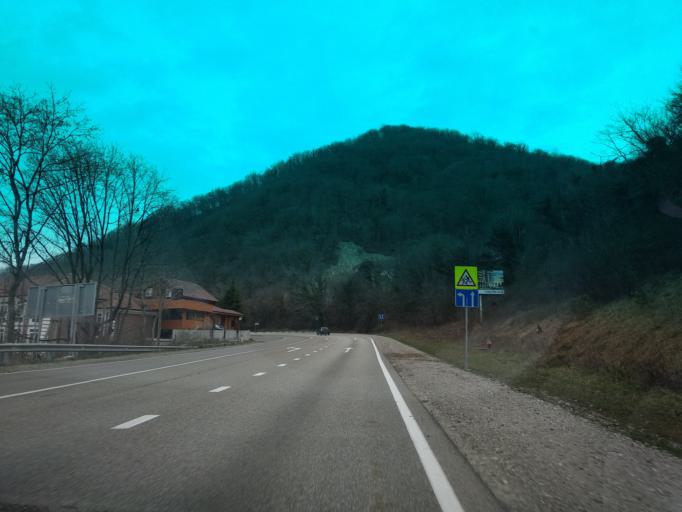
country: RU
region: Krasnodarskiy
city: Ol'ginka
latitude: 44.1941
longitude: 38.8906
